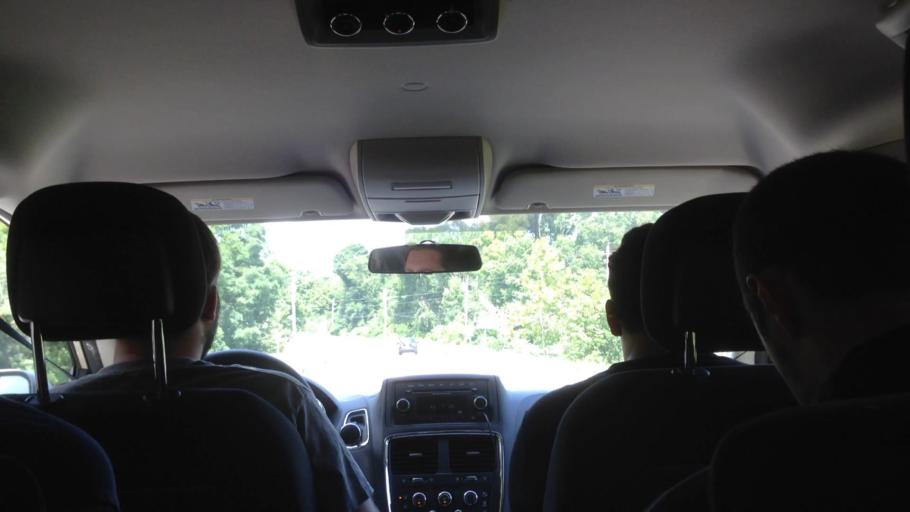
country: US
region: New York
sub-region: Dutchess County
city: Tivoli
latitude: 42.0704
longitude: -73.8944
